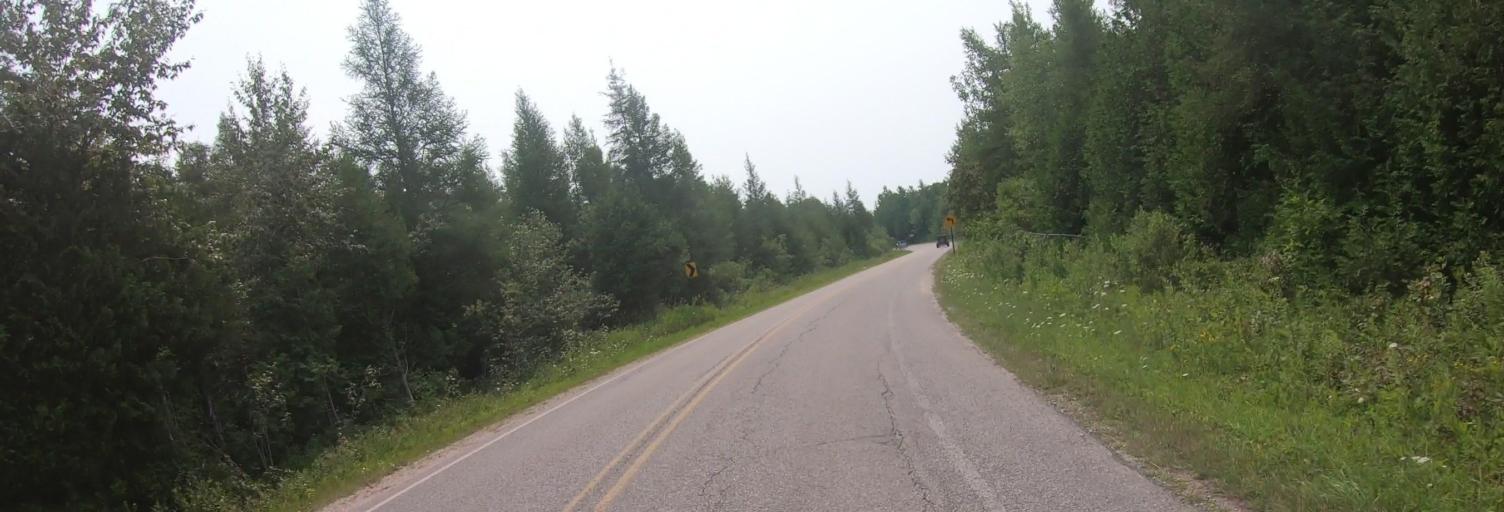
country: CA
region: Ontario
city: Thessalon
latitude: 45.9978
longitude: -83.7079
